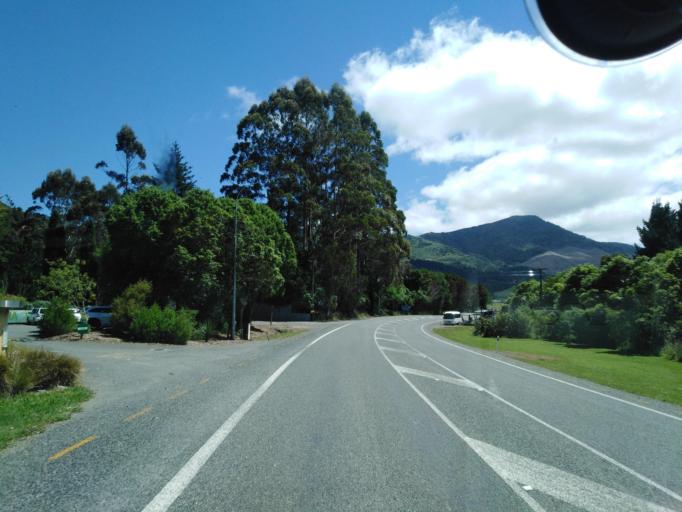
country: NZ
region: Nelson
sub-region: Nelson City
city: Nelson
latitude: -41.2164
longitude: 173.3954
